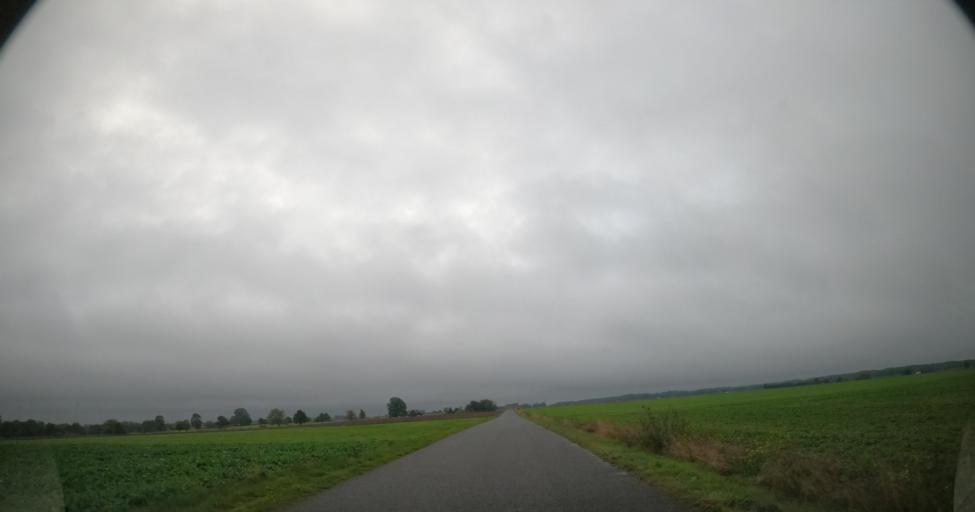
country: PL
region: West Pomeranian Voivodeship
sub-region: Powiat pyrzycki
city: Kozielice
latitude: 53.1123
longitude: 14.7635
